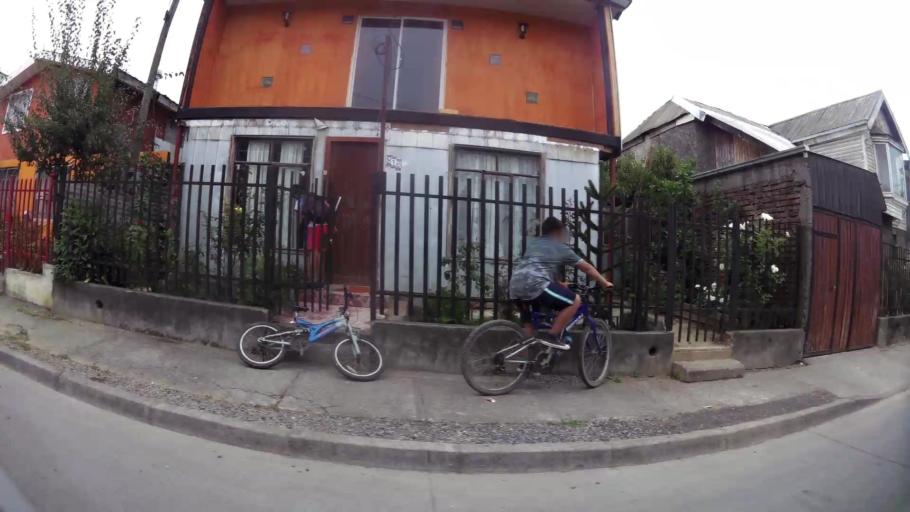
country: CL
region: Biobio
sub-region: Provincia de Concepcion
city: Concepcion
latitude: -36.8313
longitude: -73.0075
